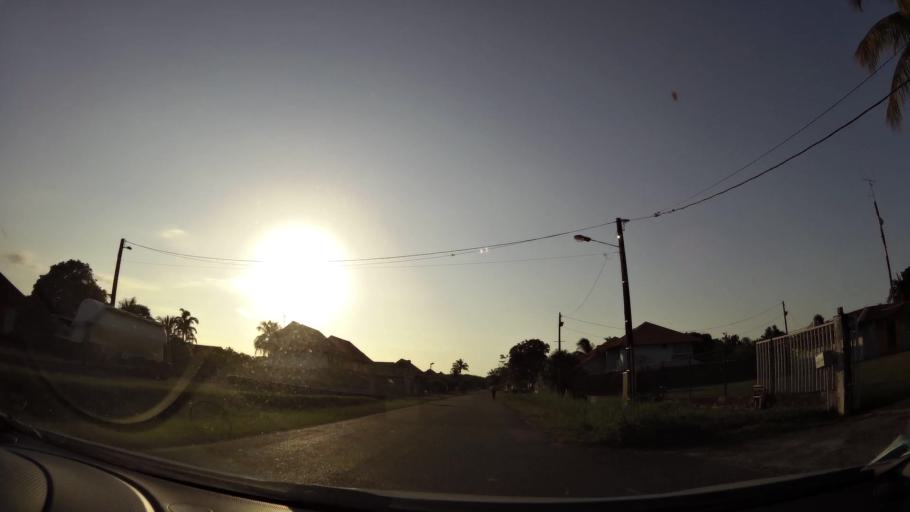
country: GF
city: Macouria
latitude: 5.0155
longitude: -52.4775
